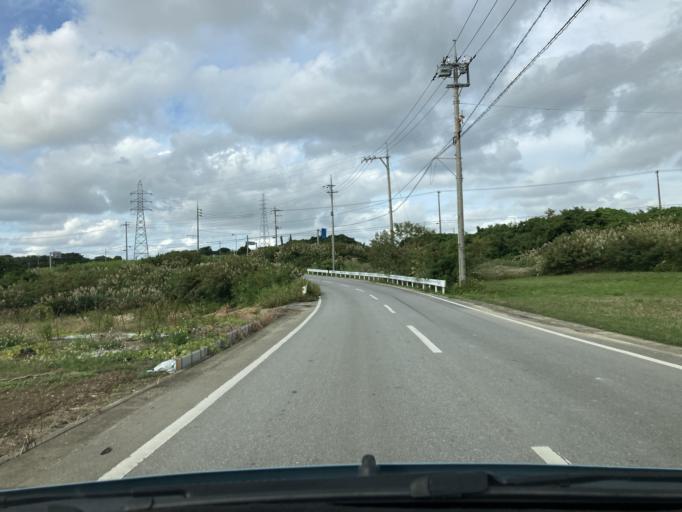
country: JP
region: Okinawa
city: Itoman
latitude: 26.1178
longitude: 127.6877
